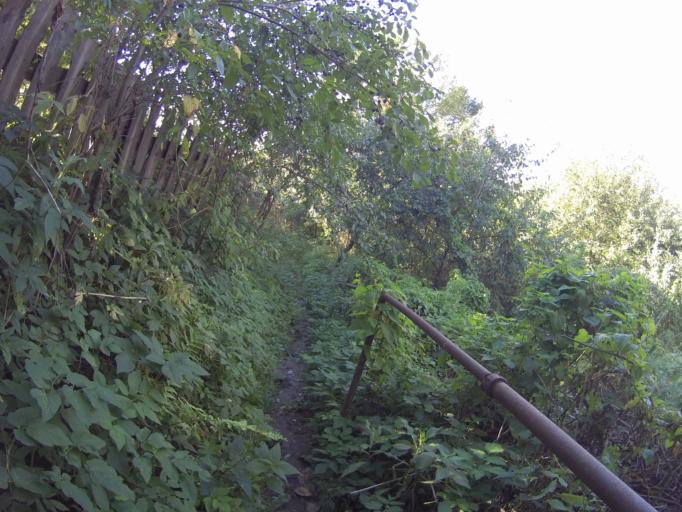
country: RU
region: Vladimir
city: Vladimir
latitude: 56.1586
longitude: 40.3647
